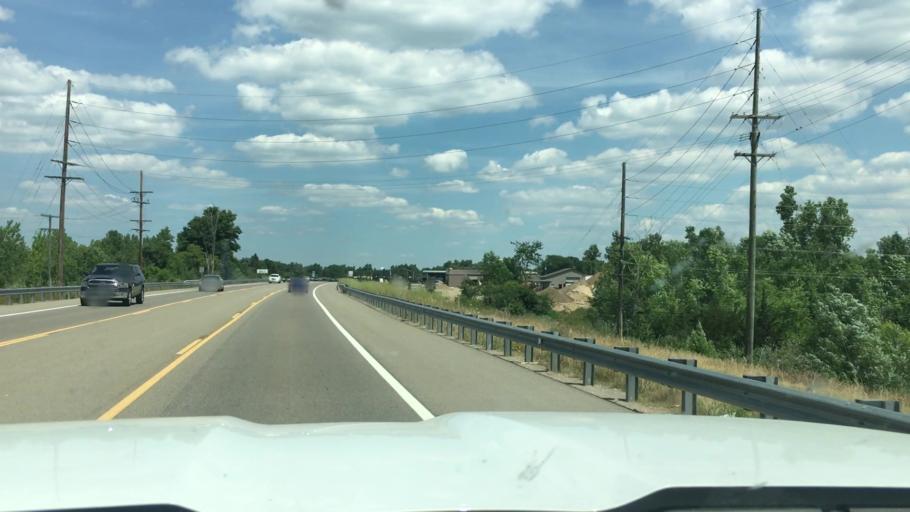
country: US
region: Michigan
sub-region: Lapeer County
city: Lapeer
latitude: 43.0675
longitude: -83.3189
